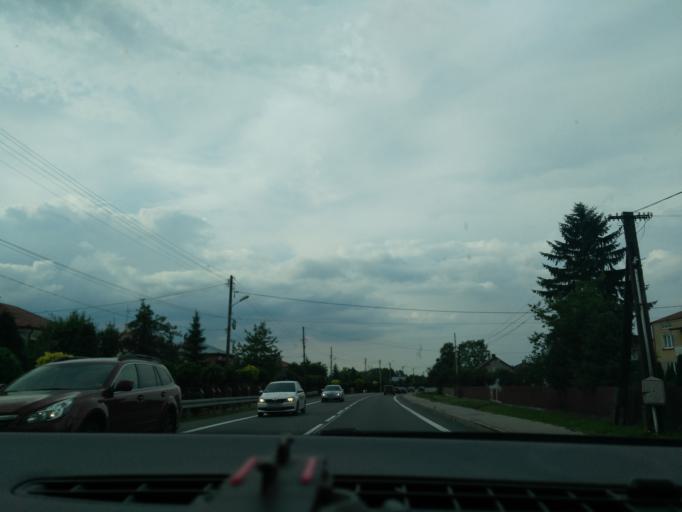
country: PL
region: Subcarpathian Voivodeship
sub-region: Powiat rzeszowski
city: Kamien
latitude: 50.3337
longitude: 22.1360
